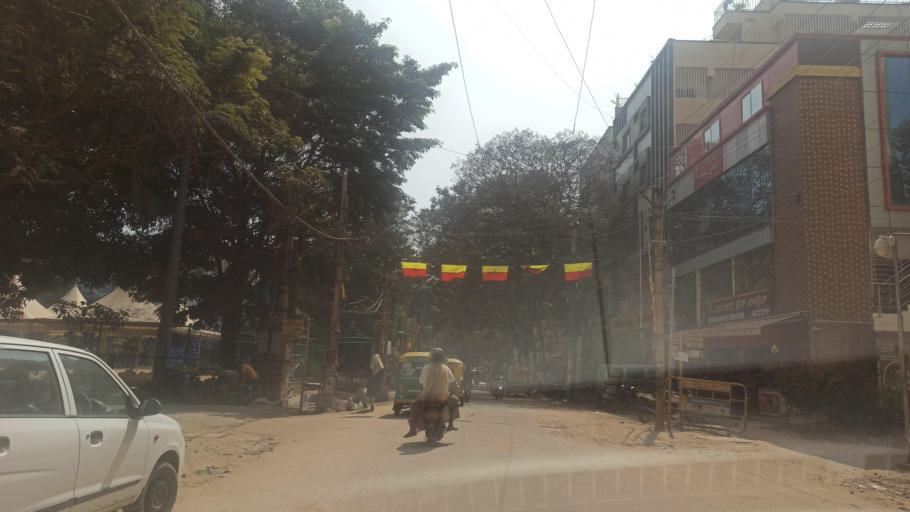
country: IN
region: Karnataka
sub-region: Bangalore Urban
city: Bangalore
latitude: 12.9630
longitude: 77.7133
